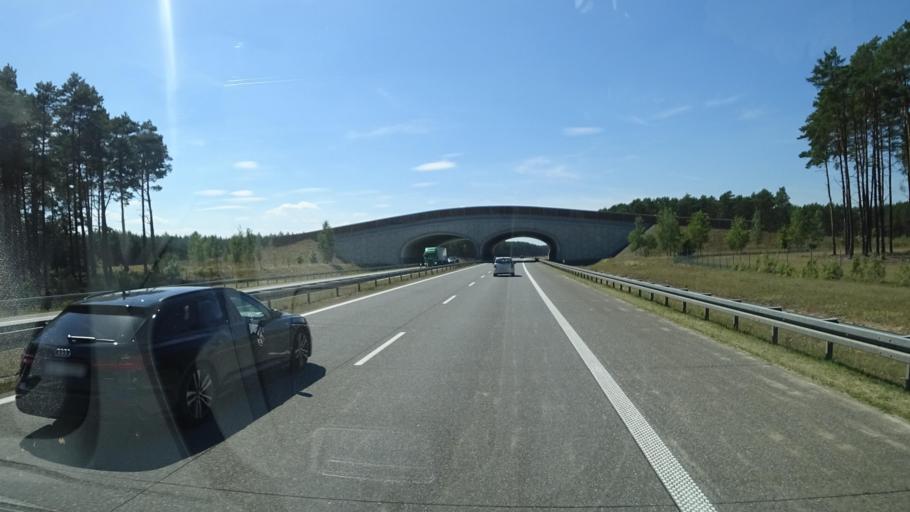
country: PL
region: Lubusz
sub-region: Powiat swiebodzinski
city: Szczaniec
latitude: 52.3007
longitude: 15.7410
